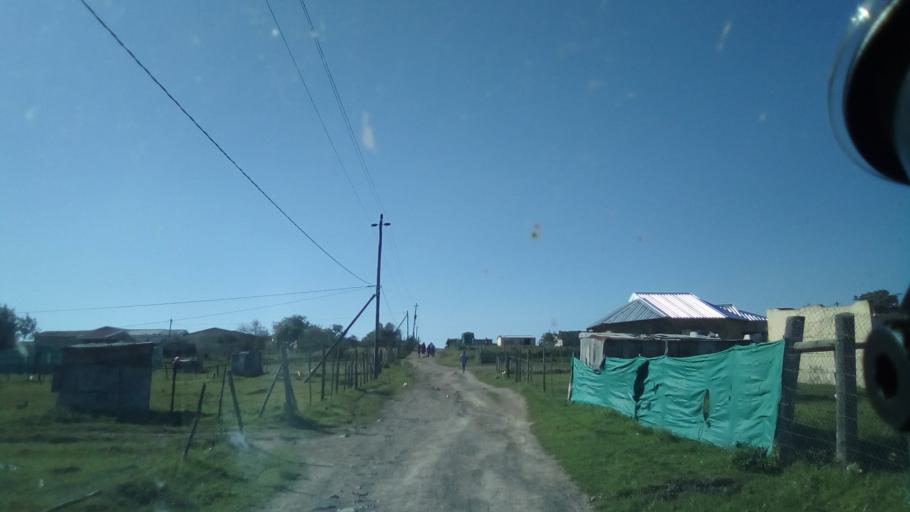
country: ZA
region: Eastern Cape
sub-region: Buffalo City Metropolitan Municipality
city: Bhisho
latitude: -32.8284
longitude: 27.3694
